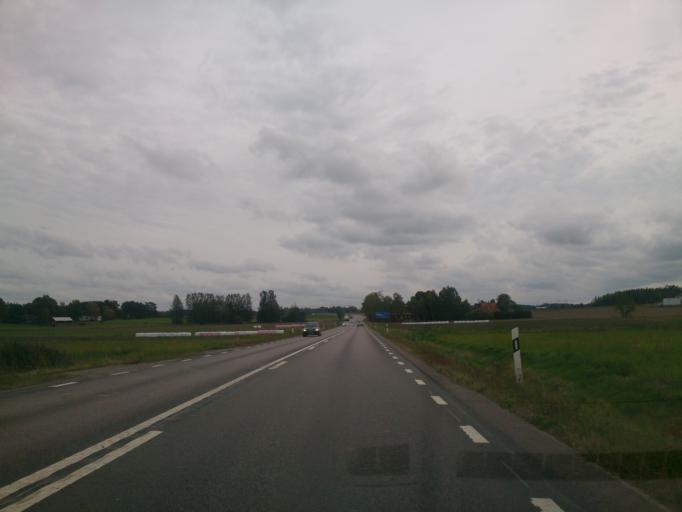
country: SE
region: OEstergoetland
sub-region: Linkopings Kommun
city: Linghem
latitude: 58.4004
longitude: 15.7555
